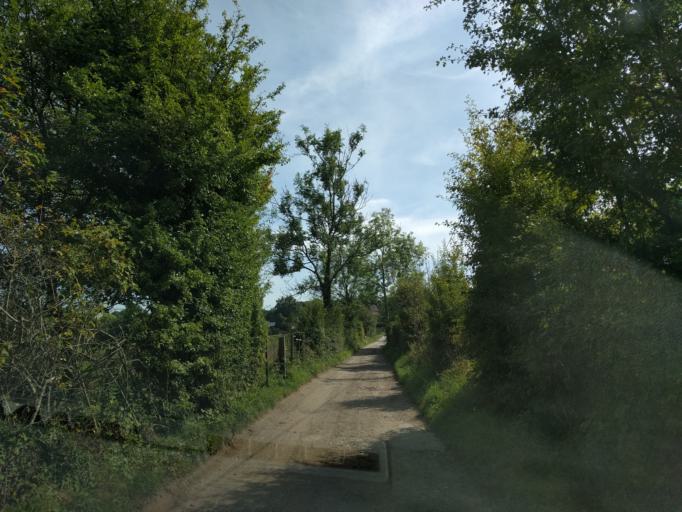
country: GB
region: England
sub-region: Surrey
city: Chilworth
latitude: 51.2182
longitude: -0.5205
